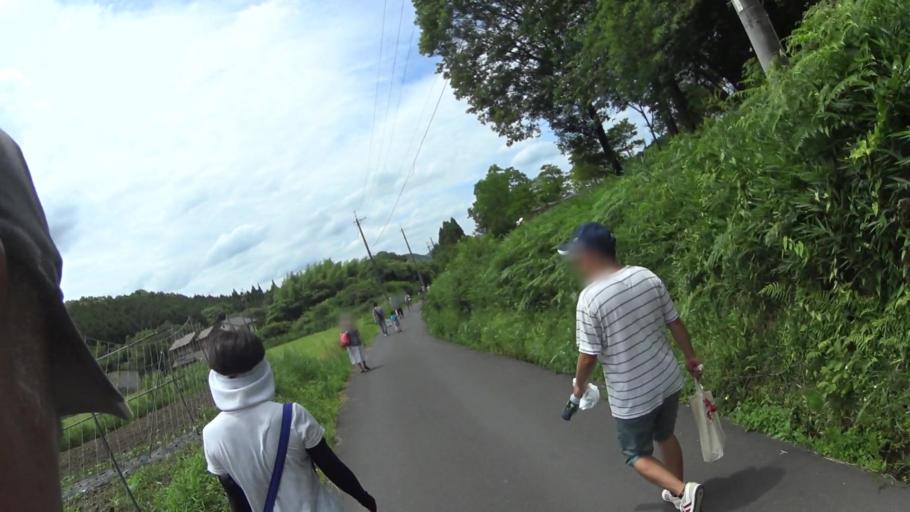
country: JP
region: Kyoto
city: Ayabe
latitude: 35.1599
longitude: 135.4167
